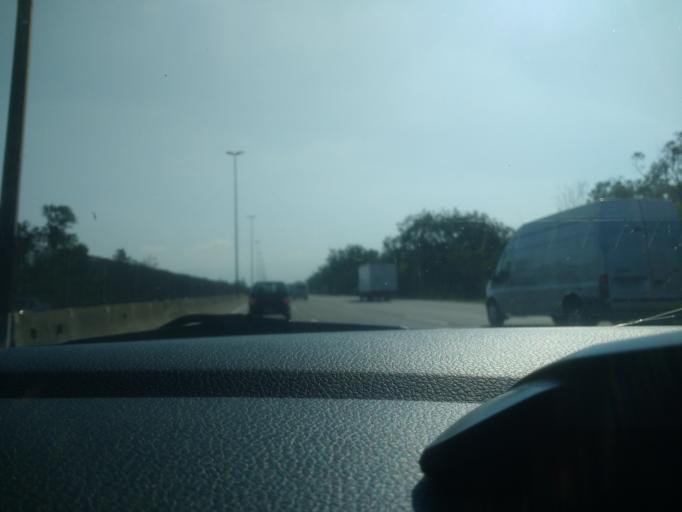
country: BR
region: Rio de Janeiro
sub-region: Duque De Caxias
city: Duque de Caxias
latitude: -22.7359
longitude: -43.2885
